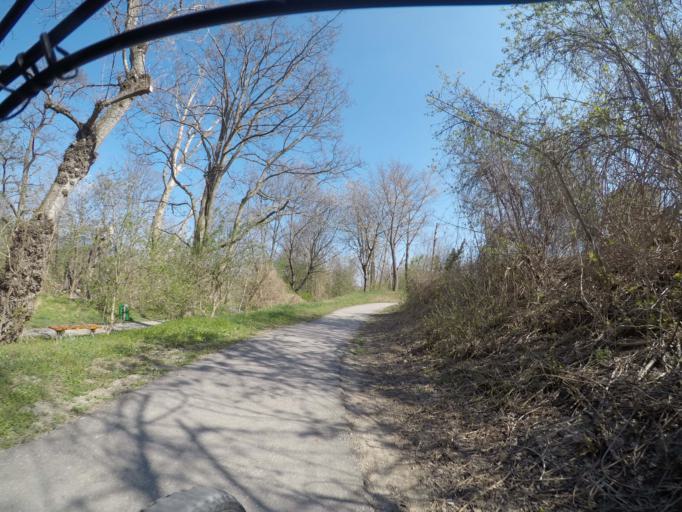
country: AT
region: Lower Austria
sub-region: Politischer Bezirk Modling
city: Biedermannsdorf
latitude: 48.0827
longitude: 16.3300
